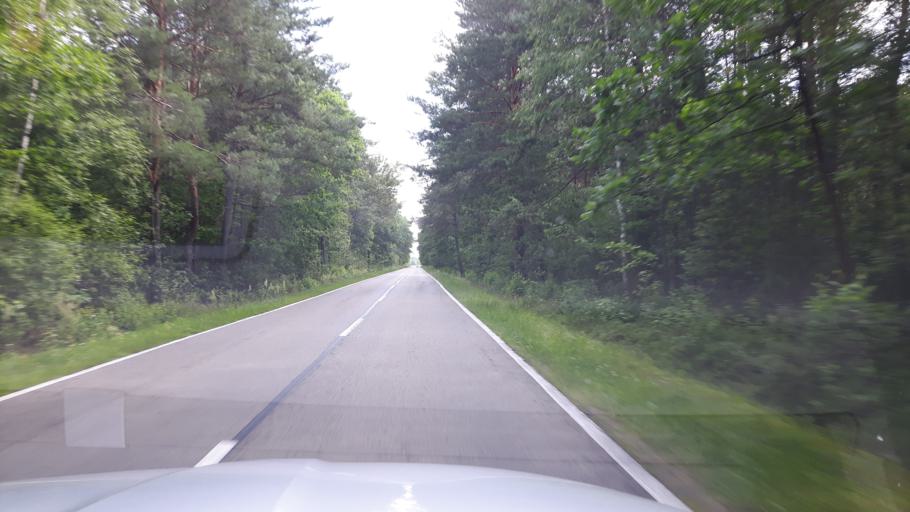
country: PL
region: Masovian Voivodeship
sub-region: Powiat wolominski
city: Strachowka
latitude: 52.4316
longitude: 21.5420
